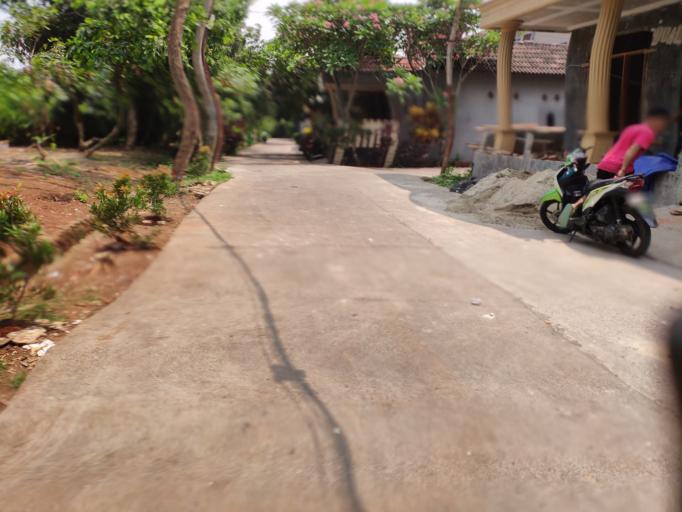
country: ID
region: West Java
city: Sawangan
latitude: -6.3715
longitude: 106.7927
